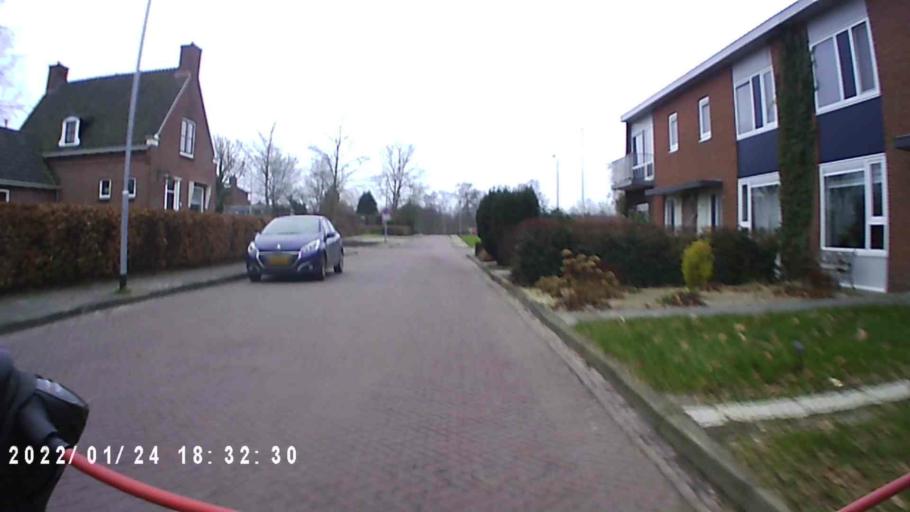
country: NL
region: Groningen
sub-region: Gemeente De Marne
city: Ulrum
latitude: 53.3589
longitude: 6.3355
